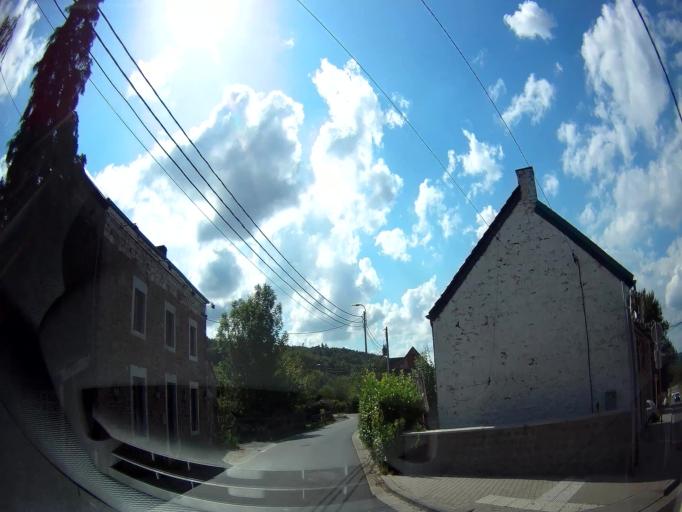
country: BE
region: Wallonia
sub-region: Province de Namur
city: Yvoir
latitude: 50.3539
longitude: 4.8960
